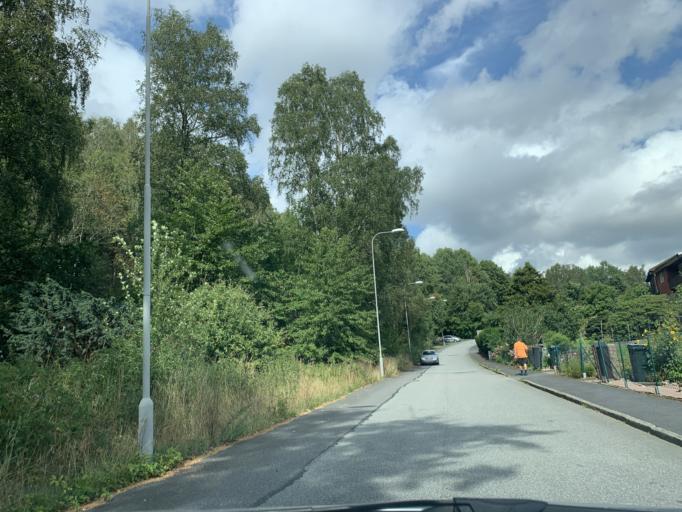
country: SE
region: Vaestra Goetaland
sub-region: Goteborg
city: Eriksbo
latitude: 57.7531
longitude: 12.0470
